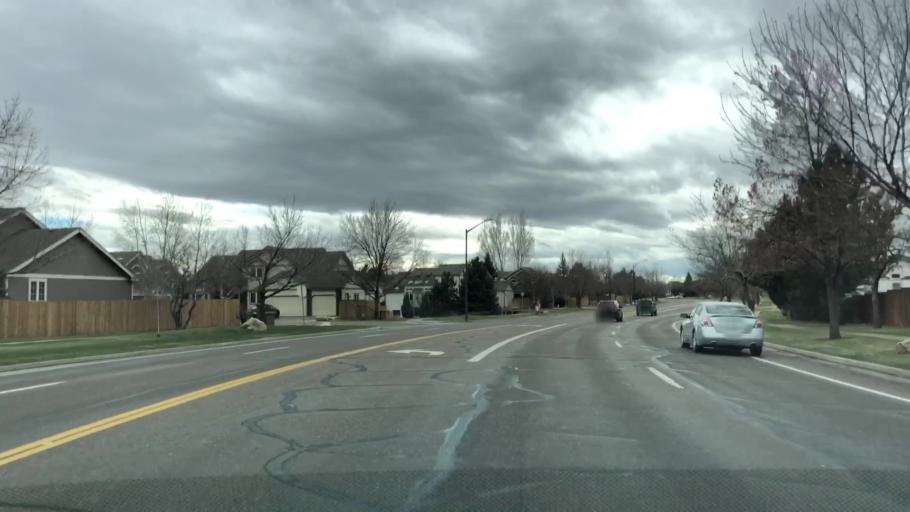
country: US
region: Colorado
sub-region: Larimer County
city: Fort Collins
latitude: 40.5287
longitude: -105.1103
